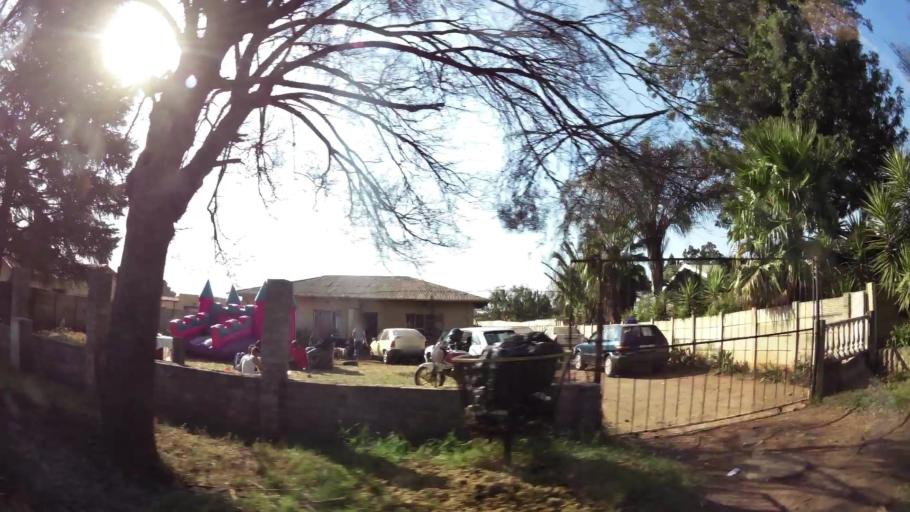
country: ZA
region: Gauteng
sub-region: West Rand District Municipality
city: Randfontein
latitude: -26.1846
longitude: 27.6921
